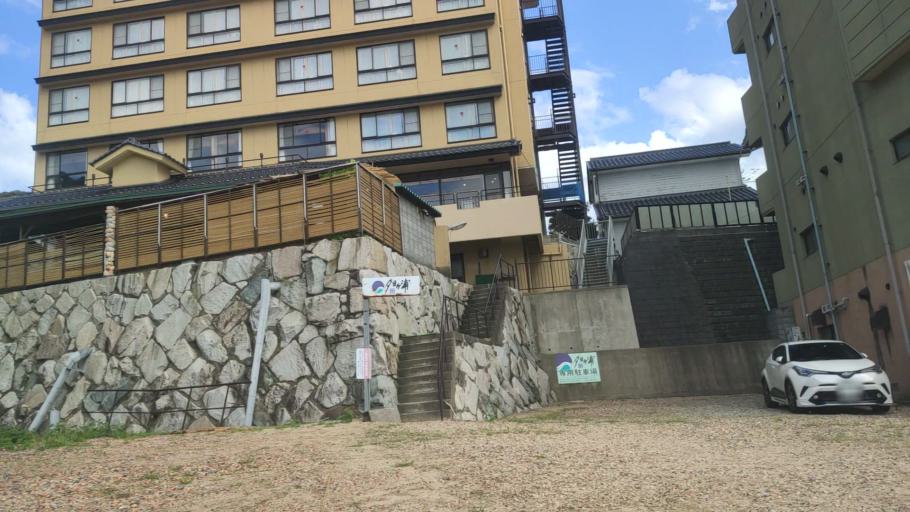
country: JP
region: Hyogo
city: Toyooka
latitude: 35.6687
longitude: 134.9681
